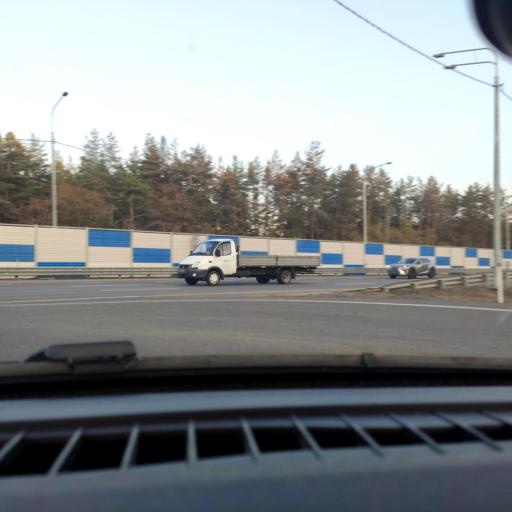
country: RU
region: Voronezj
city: Podgornoye
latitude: 51.7428
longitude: 39.1821
